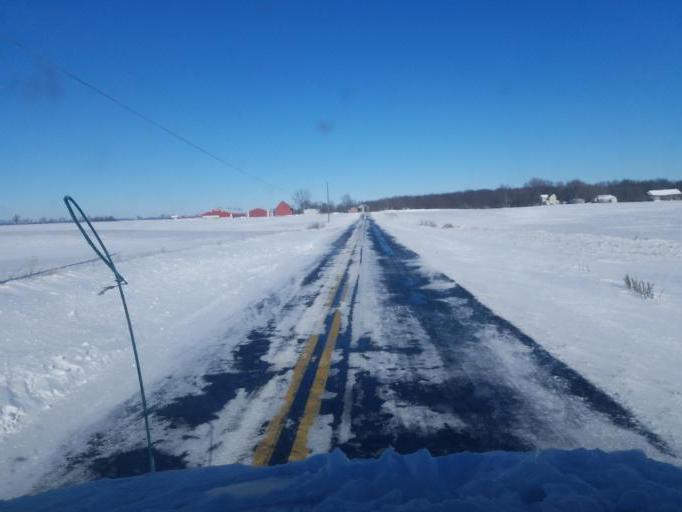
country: US
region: Ohio
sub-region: Delaware County
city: Delaware
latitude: 40.2893
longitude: -82.9878
